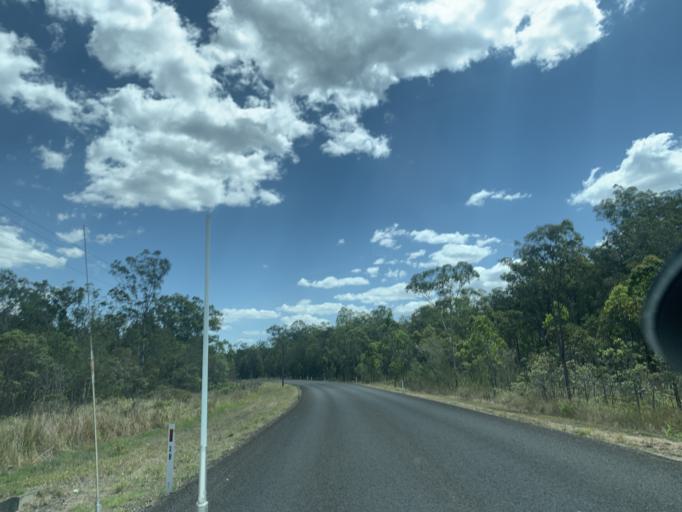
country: AU
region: Queensland
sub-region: Tablelands
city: Atherton
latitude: -17.3132
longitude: 145.4529
